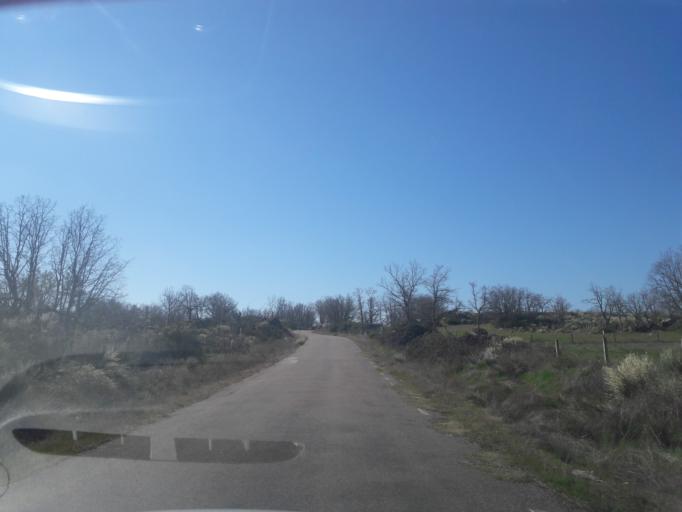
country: ES
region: Castille and Leon
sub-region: Provincia de Salamanca
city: Valsalabroso
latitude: 41.1291
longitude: -6.4823
